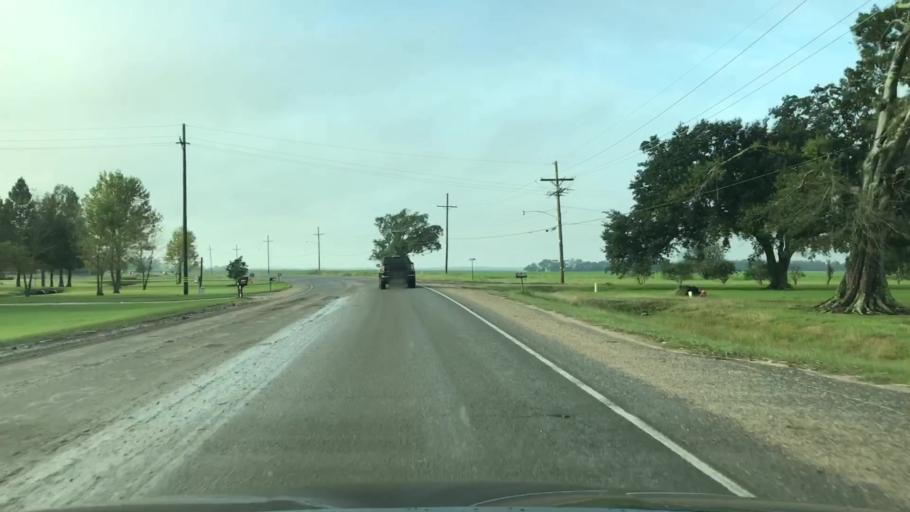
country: US
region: Louisiana
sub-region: Terrebonne Parish
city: Gray
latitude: 29.6639
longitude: -90.8199
